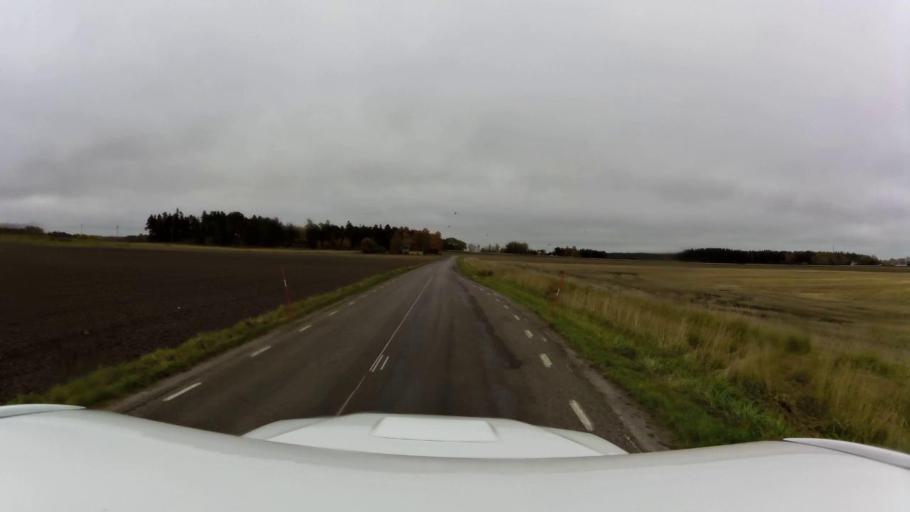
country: SE
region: OEstergoetland
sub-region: Linkopings Kommun
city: Linghem
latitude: 58.4350
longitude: 15.7170
